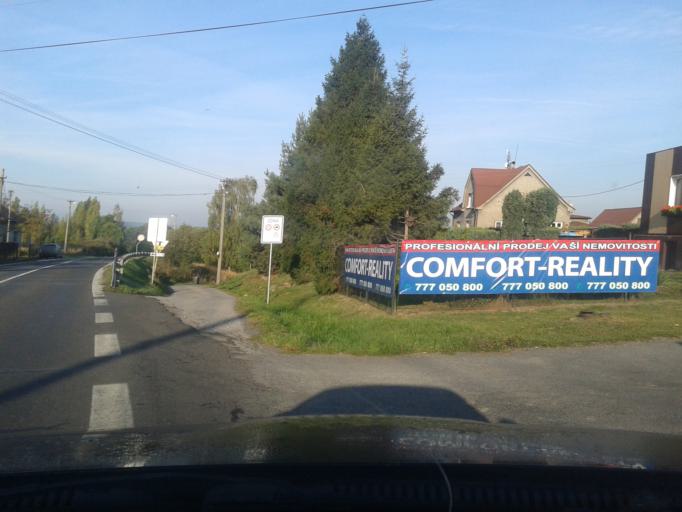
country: CZ
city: Rychvald
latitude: 49.8676
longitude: 18.3689
